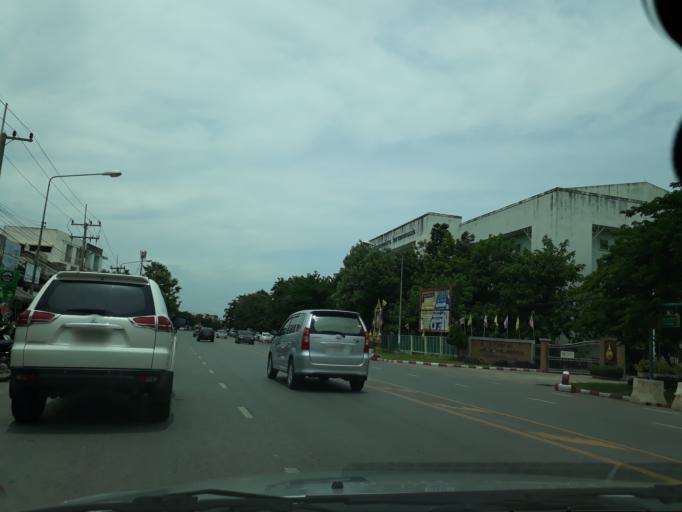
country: TH
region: Khon Kaen
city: Khon Kaen
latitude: 16.4336
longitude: 102.8639
